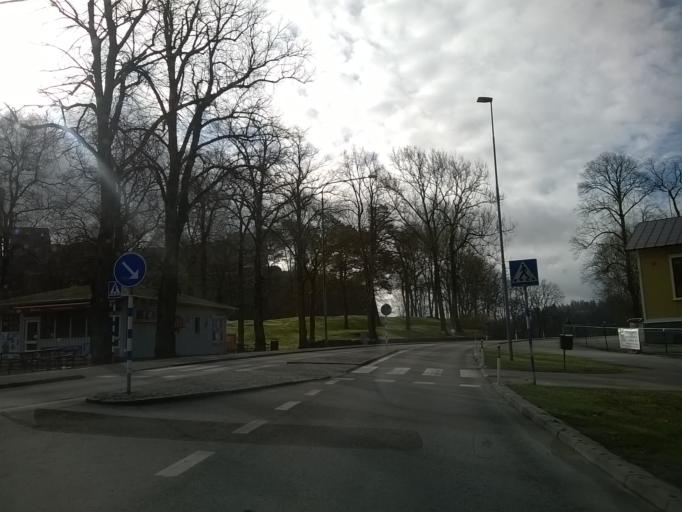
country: SE
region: Vaestra Goetaland
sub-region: Kungalvs Kommun
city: Kungalv
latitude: 57.8628
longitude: 11.9964
